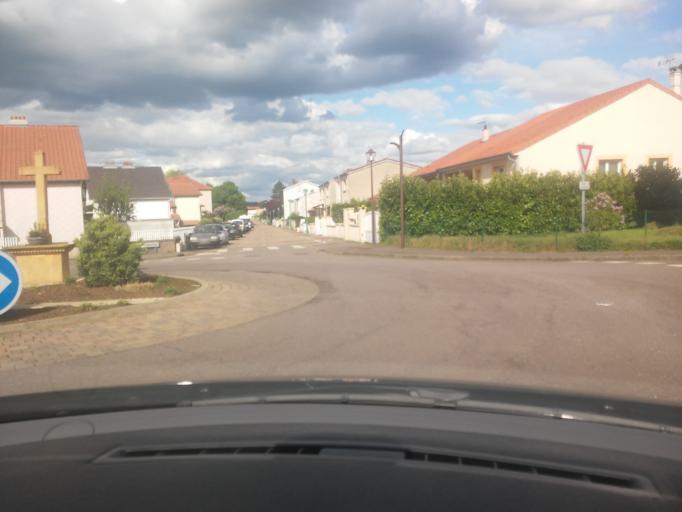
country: FR
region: Lorraine
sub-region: Departement de la Moselle
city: Amanvillers
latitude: 49.1653
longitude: 6.0401
